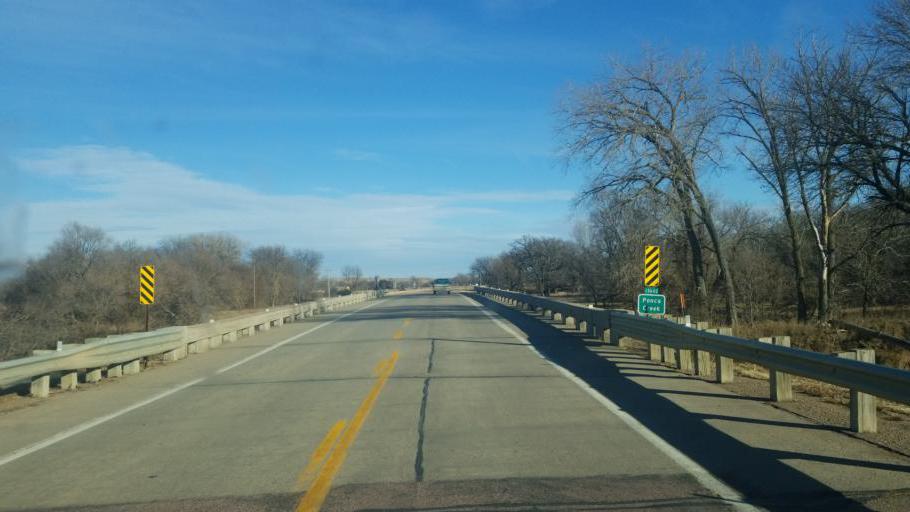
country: US
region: South Dakota
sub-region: Charles Mix County
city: Wagner
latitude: 42.8267
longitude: -98.4666
